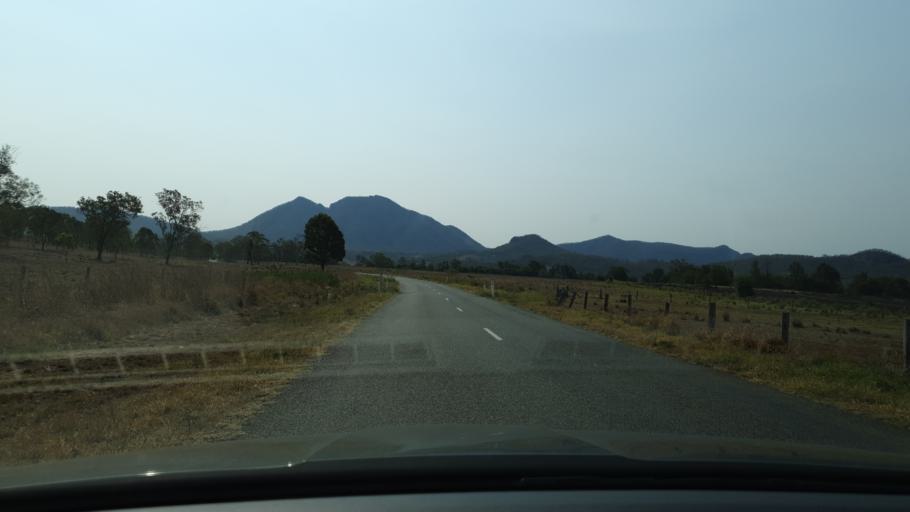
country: AU
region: Queensland
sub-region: Ipswich
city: Deebing Heights
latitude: -28.1392
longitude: 152.6023
